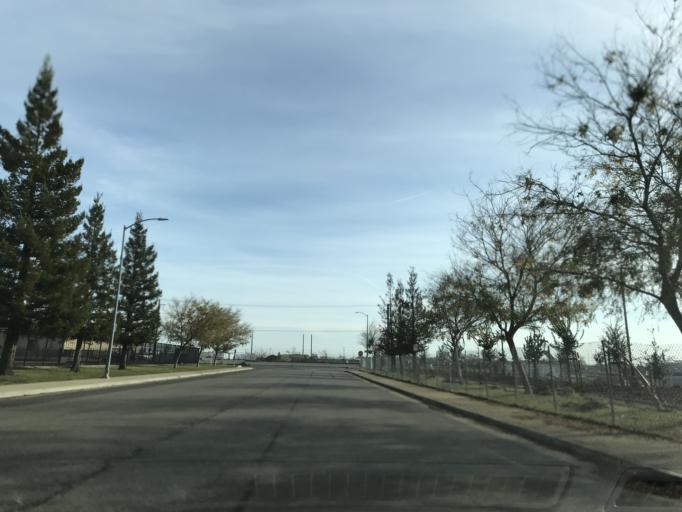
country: US
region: California
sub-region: Sacramento County
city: Arden-Arcade
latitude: 38.6422
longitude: -121.4073
